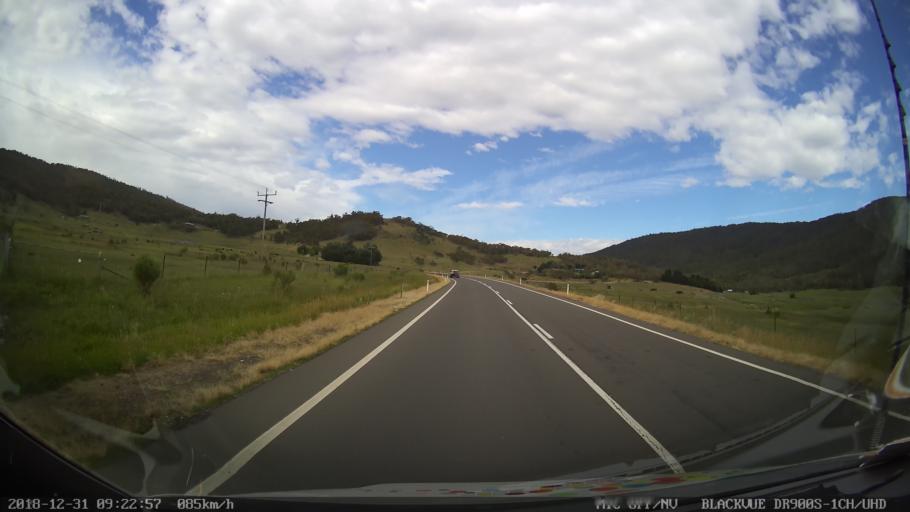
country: AU
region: New South Wales
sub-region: Snowy River
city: Jindabyne
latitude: -36.4372
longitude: 148.5402
